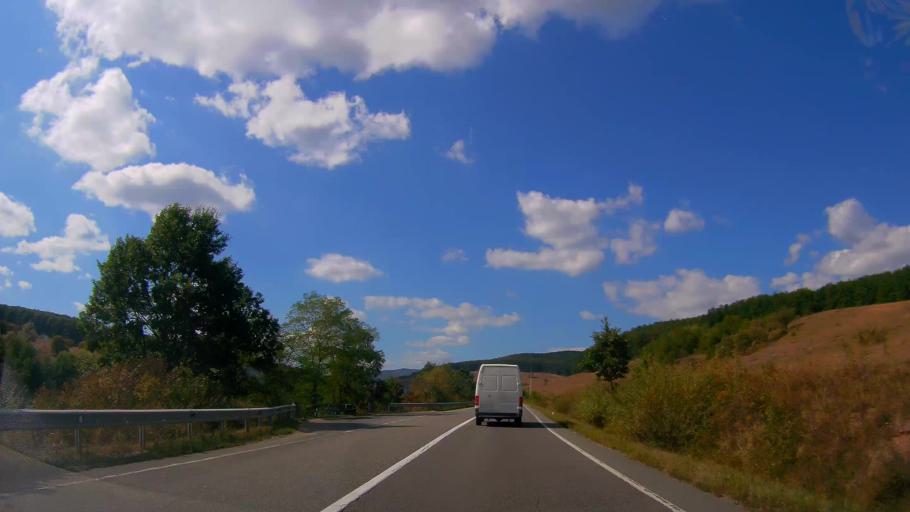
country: RO
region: Salaj
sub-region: Comuna Romanasi
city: Romanasi
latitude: 47.1212
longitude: 23.1611
